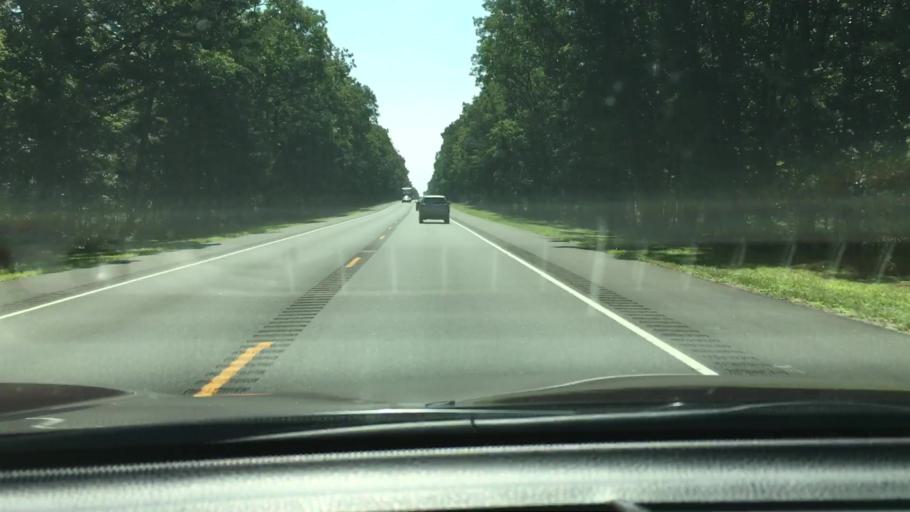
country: US
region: New Jersey
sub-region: Cumberland County
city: Laurel Lake
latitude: 39.3452
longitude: -74.9002
